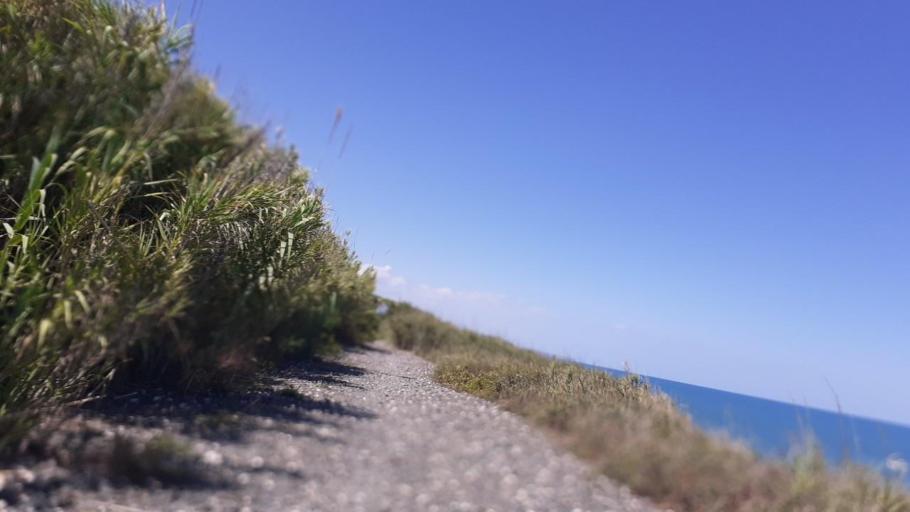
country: IT
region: Abruzzo
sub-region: Provincia di Chieti
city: Torino di Sangro
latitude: 42.2183
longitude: 14.5751
